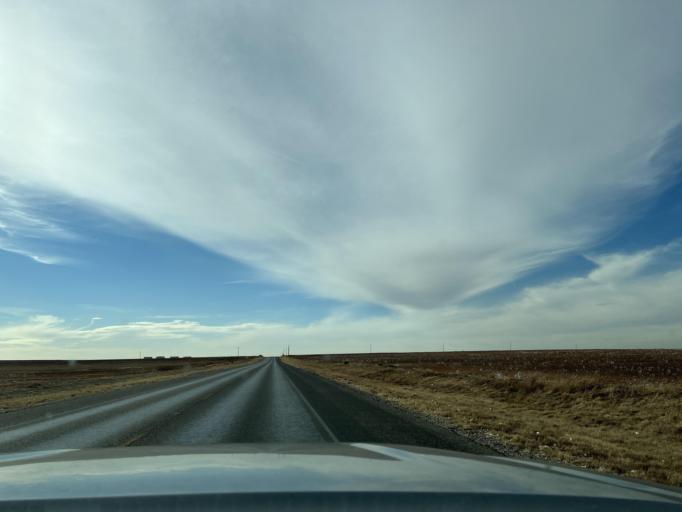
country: US
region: Texas
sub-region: Fisher County
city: Roby
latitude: 32.7417
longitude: -100.4509
